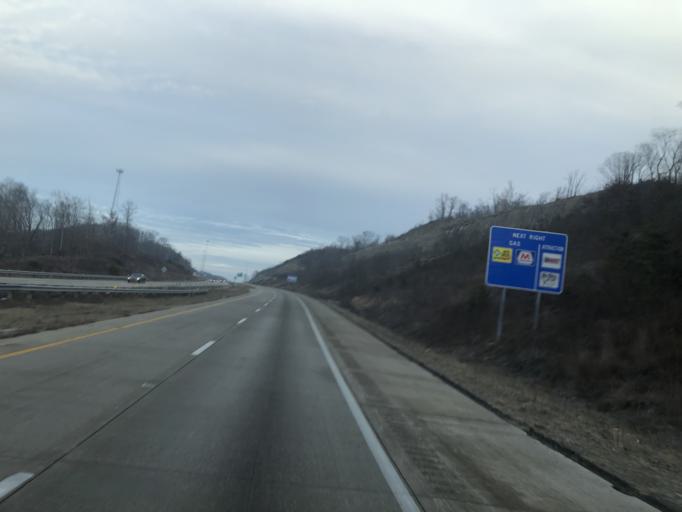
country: US
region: Ohio
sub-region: Athens County
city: Nelsonville
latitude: 39.4336
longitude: -82.1984
